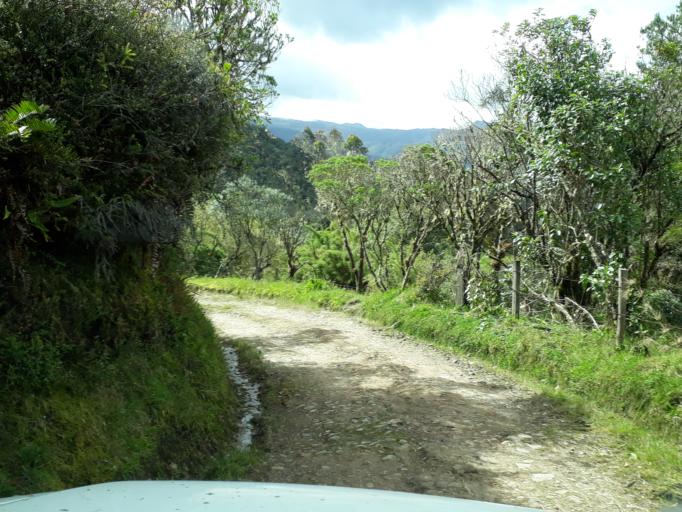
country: CO
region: Cundinamarca
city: Junin
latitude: 4.7810
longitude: -73.7747
